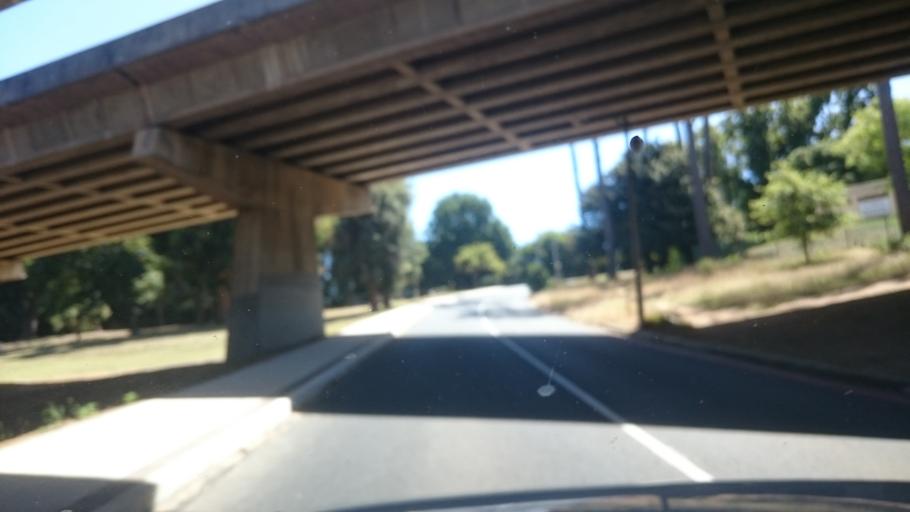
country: ZA
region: Western Cape
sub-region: City of Cape Town
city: Newlands
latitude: -34.0001
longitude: 18.4502
